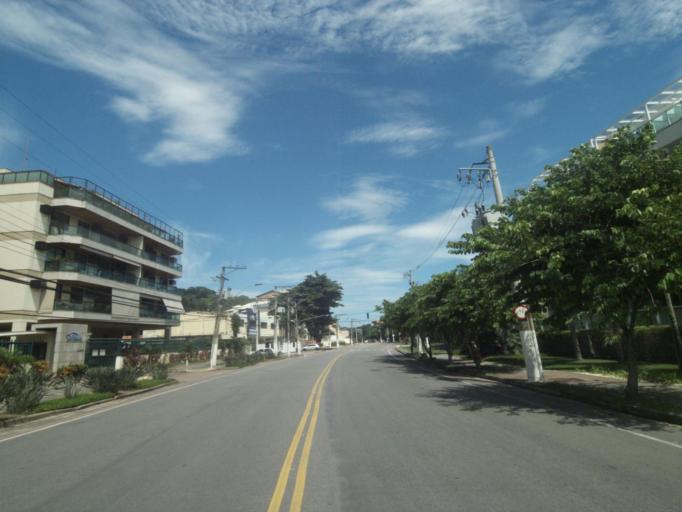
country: BR
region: Rio de Janeiro
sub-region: Niteroi
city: Niteroi
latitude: -22.9642
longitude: -43.0327
